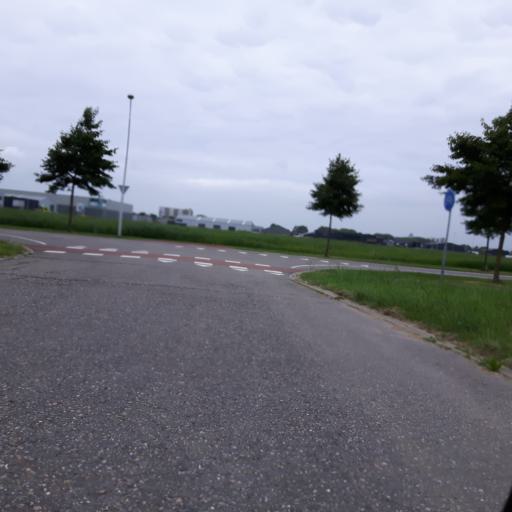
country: NL
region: Zeeland
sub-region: Gemeente Goes
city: Goes
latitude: 51.4836
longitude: 3.8844
